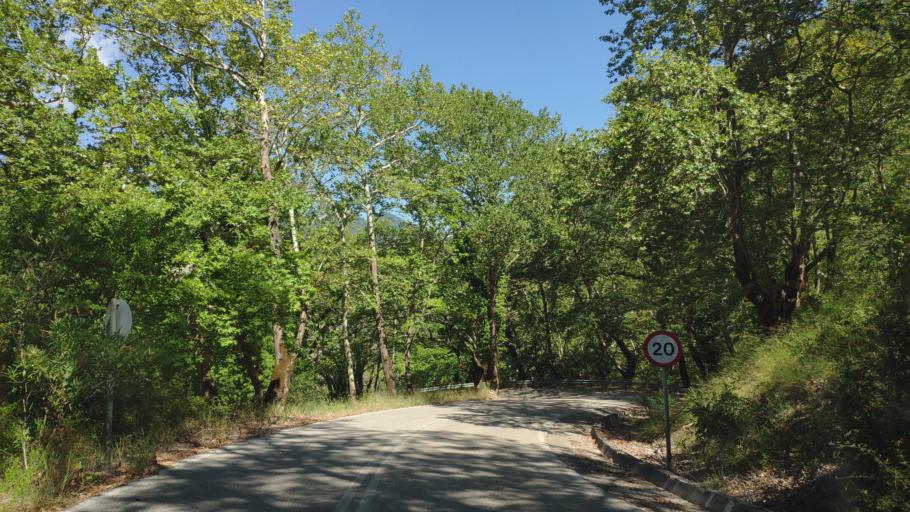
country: GR
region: Central Greece
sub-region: Nomos Evrytanias
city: Kerasochori
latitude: 39.0214
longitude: 21.6011
